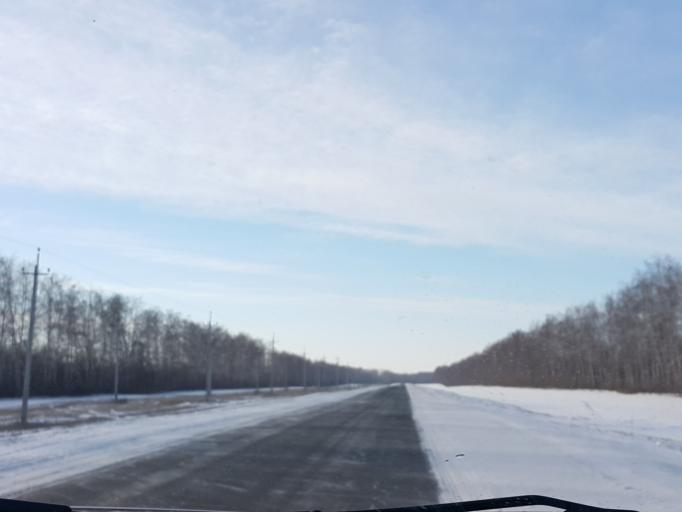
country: RU
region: Tambov
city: Znamenka
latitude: 52.3881
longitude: 41.3444
